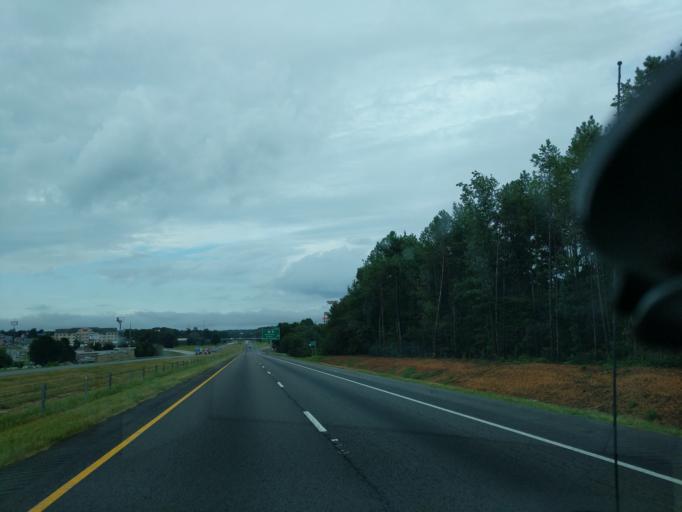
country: US
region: Georgia
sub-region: Jackson County
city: Commerce
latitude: 34.2509
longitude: -83.4701
